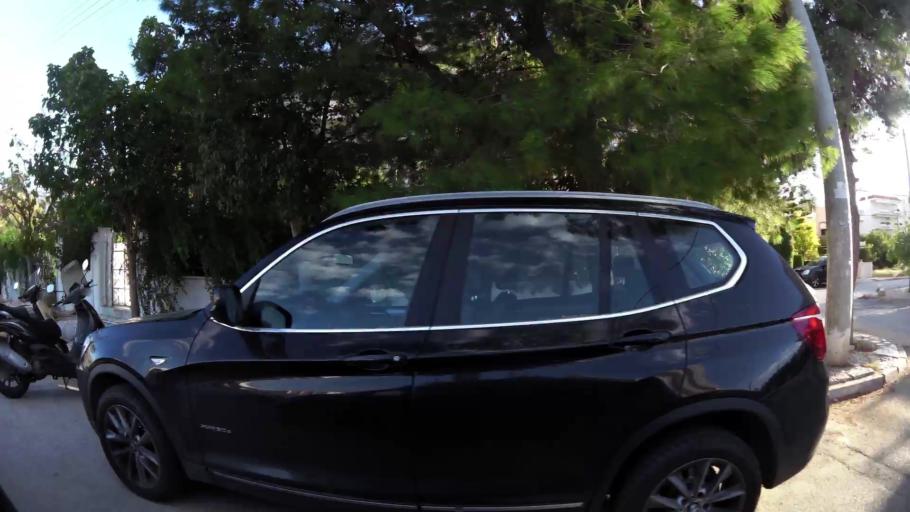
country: GR
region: Attica
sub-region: Nomarchia Athinas
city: Elliniko
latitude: 37.8824
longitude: 23.7465
